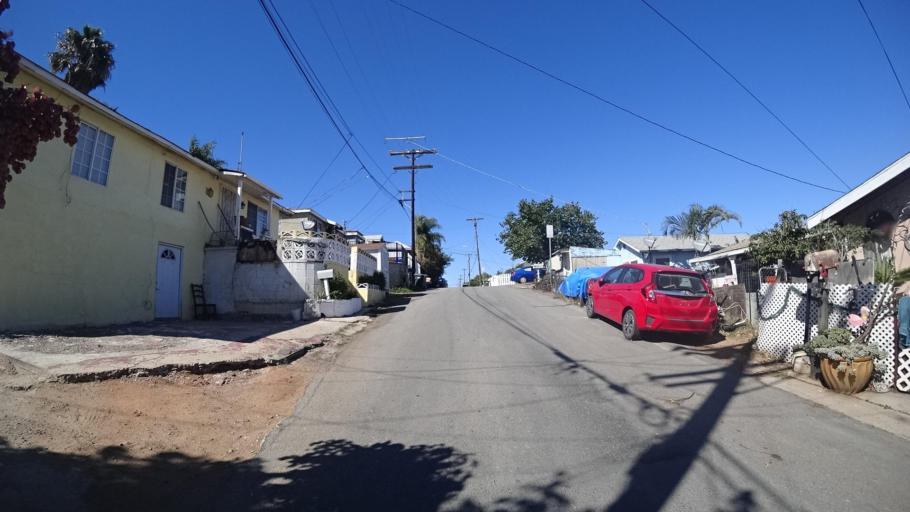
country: US
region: California
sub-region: San Diego County
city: National City
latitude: 32.6695
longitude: -117.0704
